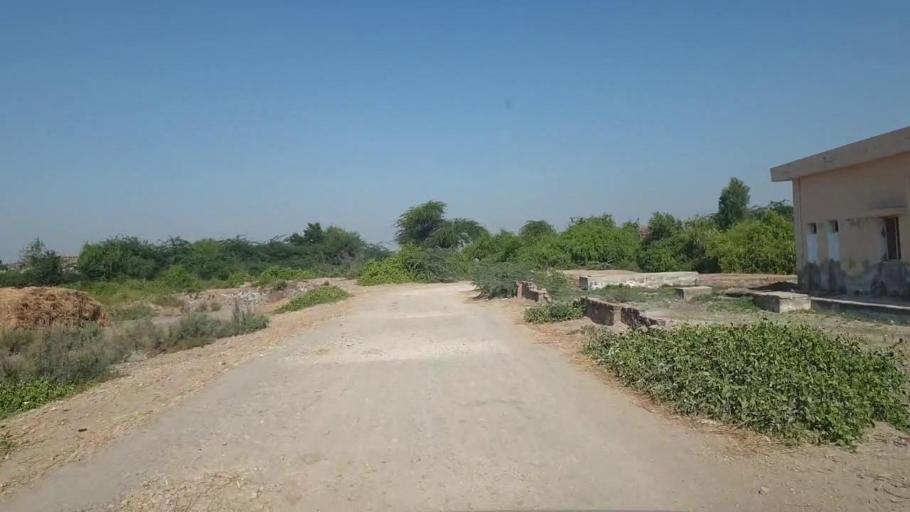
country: PK
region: Sindh
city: Talhar
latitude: 24.7913
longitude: 68.7971
